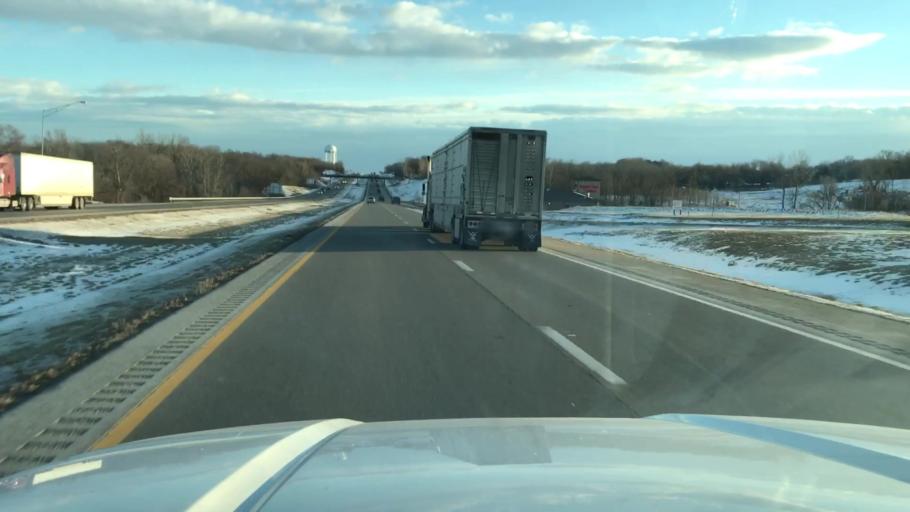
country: US
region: Missouri
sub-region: Andrew County
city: Country Club Village
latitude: 39.8124
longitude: -94.8030
